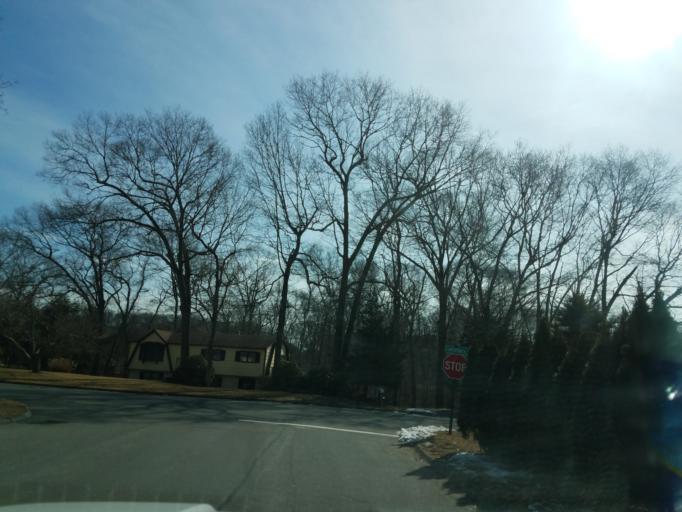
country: US
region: Connecticut
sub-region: New London County
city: Pawcatuck
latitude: 41.3982
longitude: -71.8527
